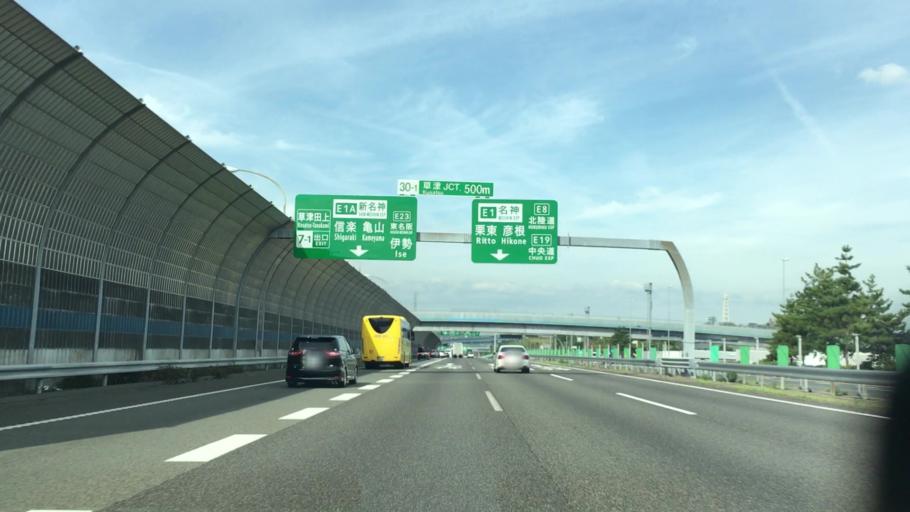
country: JP
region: Shiga Prefecture
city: Kusatsu
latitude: 34.9776
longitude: 135.9481
